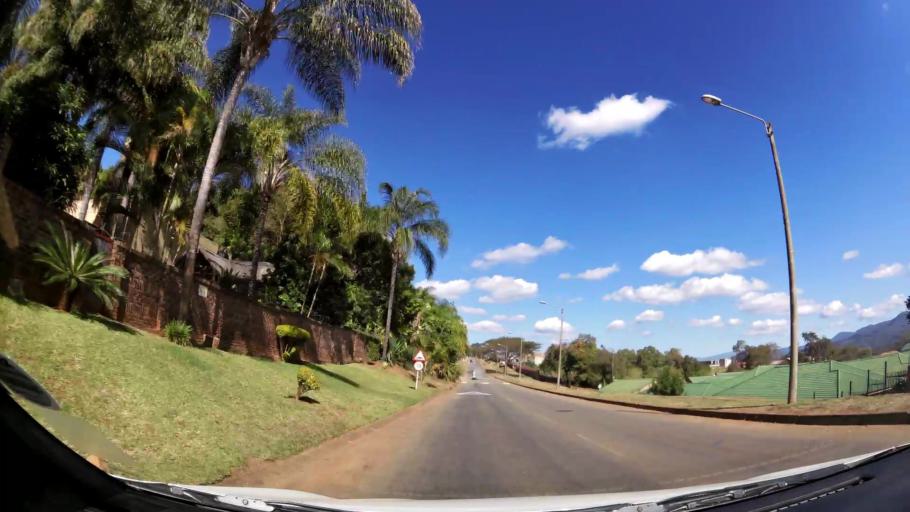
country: ZA
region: Limpopo
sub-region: Mopani District Municipality
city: Tzaneen
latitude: -23.8209
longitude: 30.1439
